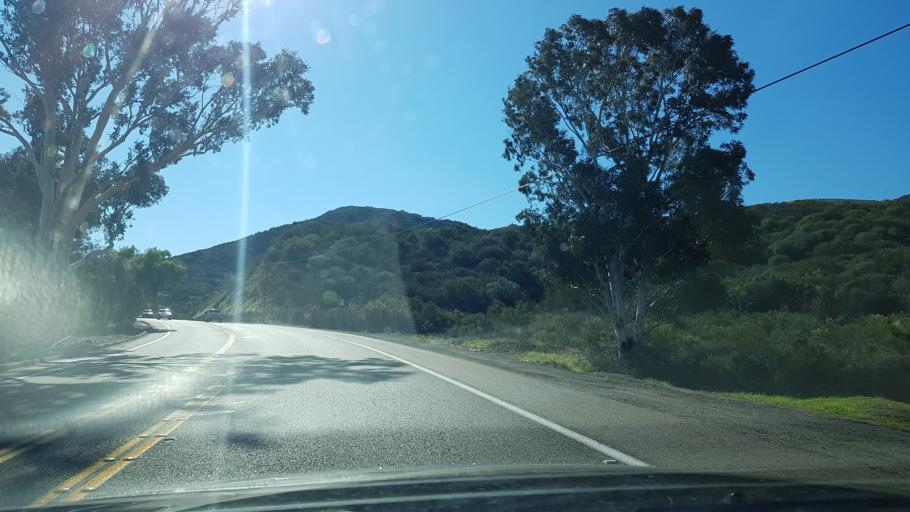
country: US
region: California
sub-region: San Diego County
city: Escondido
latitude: 33.0657
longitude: -117.1237
